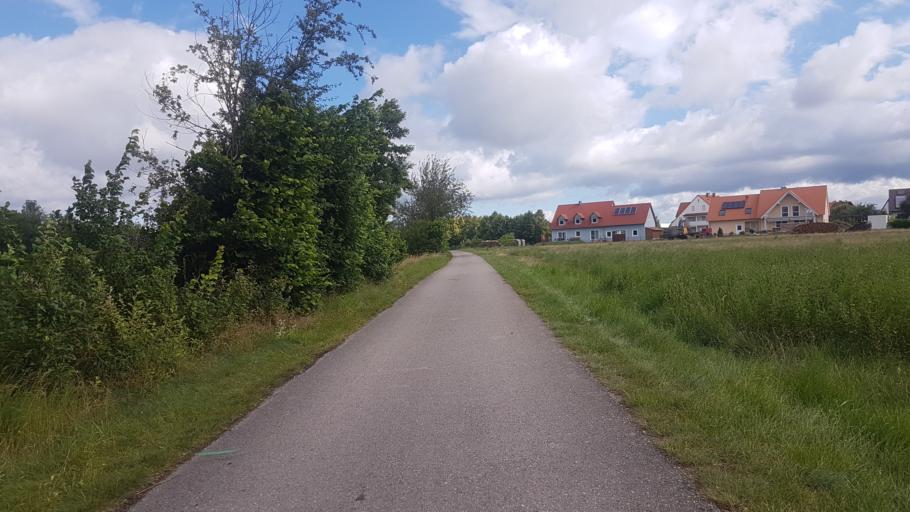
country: DE
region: Bavaria
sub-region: Regierungsbezirk Mittelfranken
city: Ornbau
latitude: 49.1662
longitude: 10.6582
